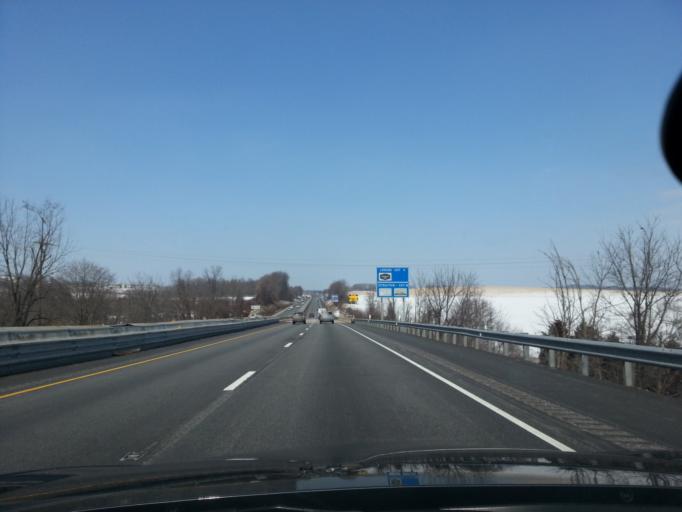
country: US
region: Pennsylvania
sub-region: York County
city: Shrewsbury
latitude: 39.7590
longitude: -76.6635
